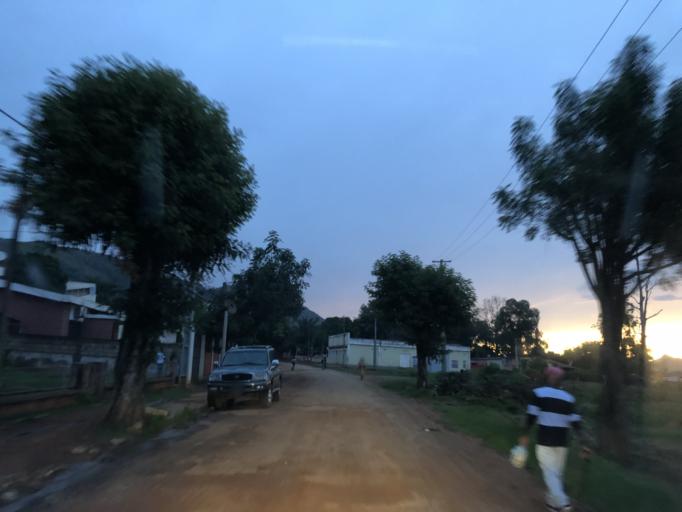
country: AO
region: Cuanza Sul
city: Uacu Cungo
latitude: -11.3636
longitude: 15.1154
